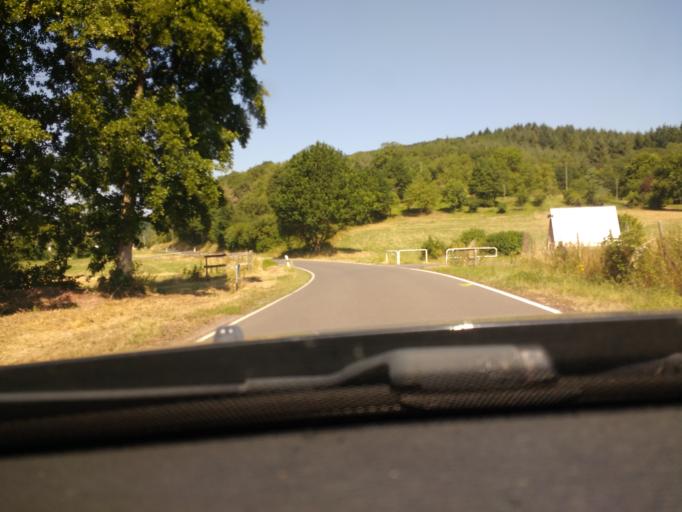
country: DE
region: Rheinland-Pfalz
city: Wittlich
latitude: 49.9962
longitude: 6.9162
